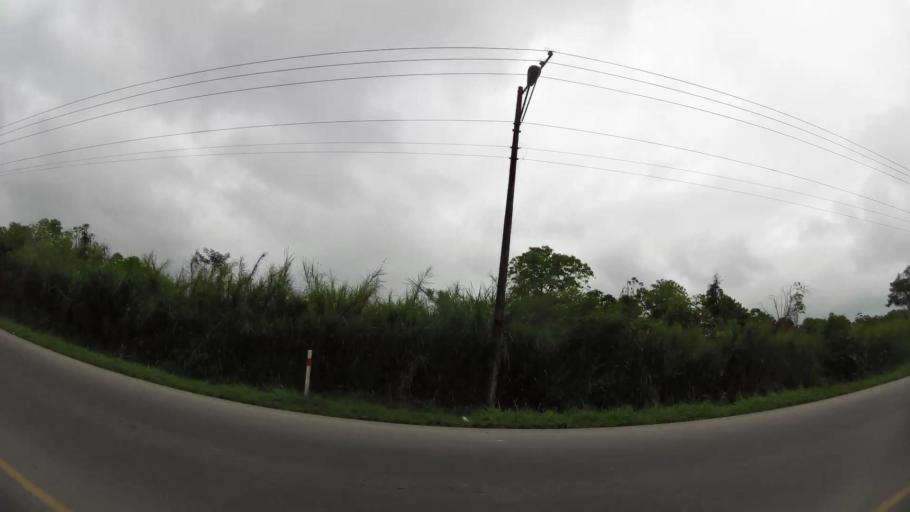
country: EC
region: Santo Domingo de los Tsachilas
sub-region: Canton Santo Domingo de los Colorados
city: Santo Domingo de los Colorados
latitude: -0.2394
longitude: -79.1520
